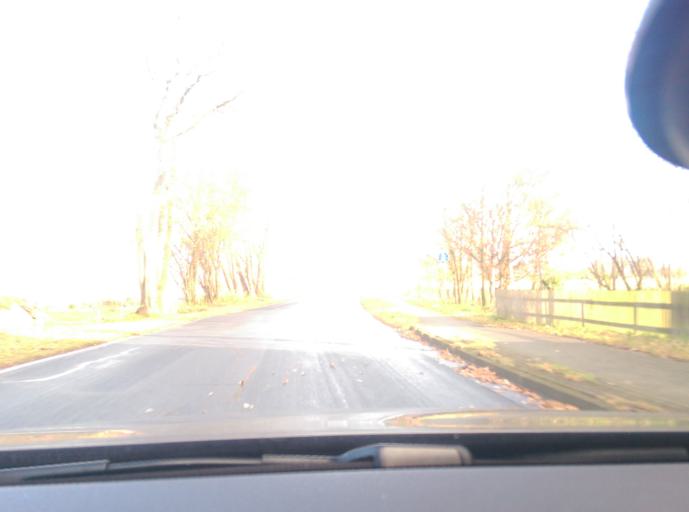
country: DE
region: Lower Saxony
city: Wietze
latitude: 52.6647
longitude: 9.7691
